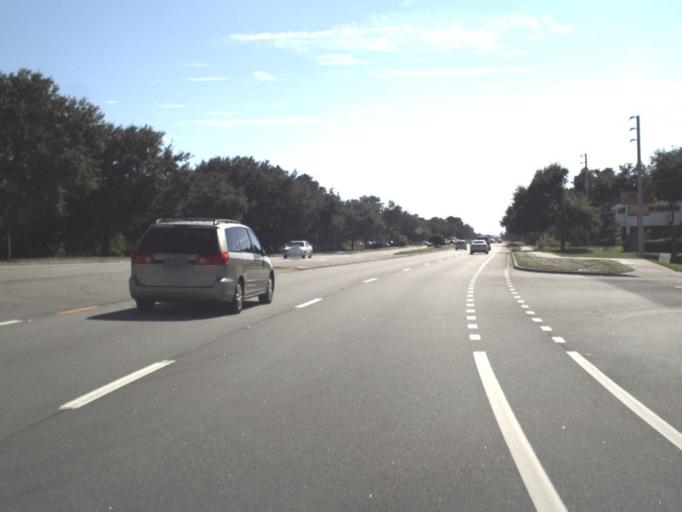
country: US
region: Florida
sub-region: Brevard County
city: South Patrick Shores
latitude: 28.2135
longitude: -80.6722
